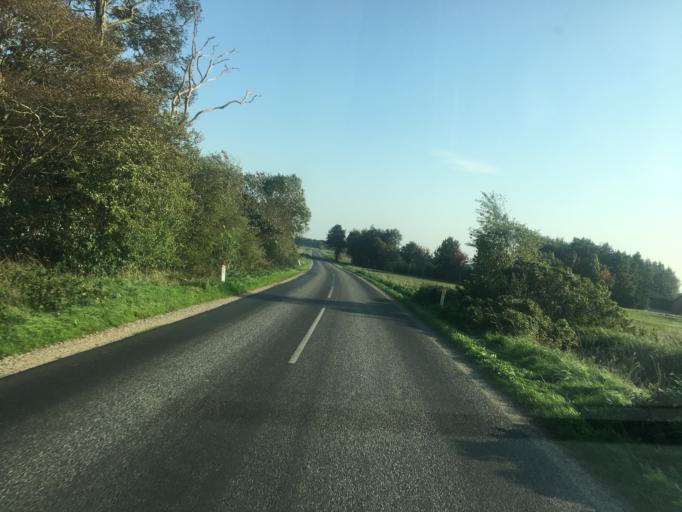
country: DE
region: Schleswig-Holstein
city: Bramstedtlund
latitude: 54.9465
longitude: 9.0610
